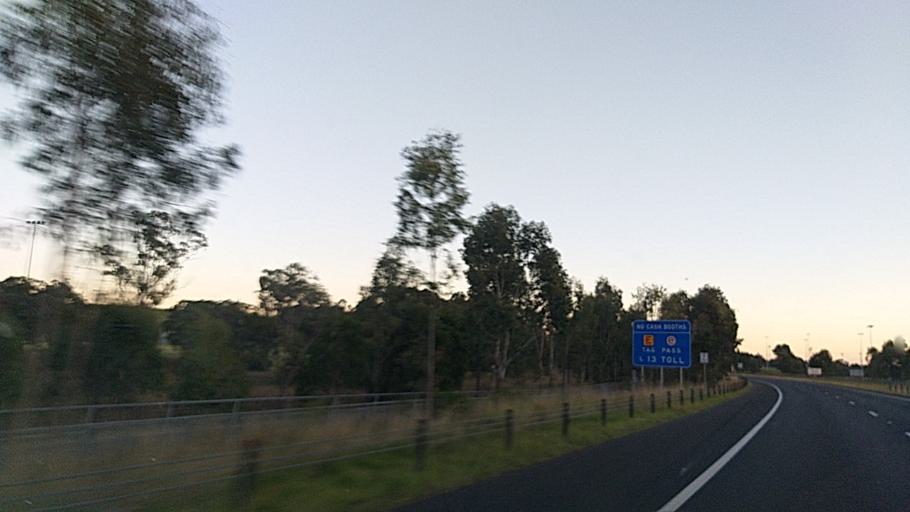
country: AU
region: New South Wales
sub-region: Blacktown
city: Doonside
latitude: -33.7789
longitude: 150.8574
